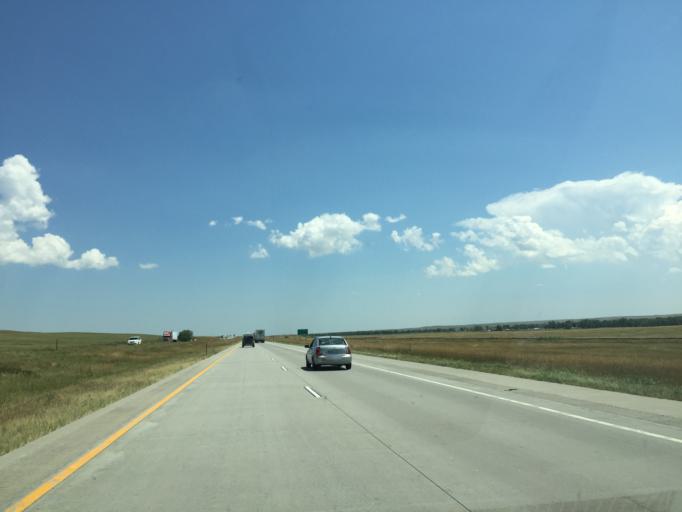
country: US
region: Colorado
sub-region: Lincoln County
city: Limon
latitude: 39.2971
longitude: -103.8057
